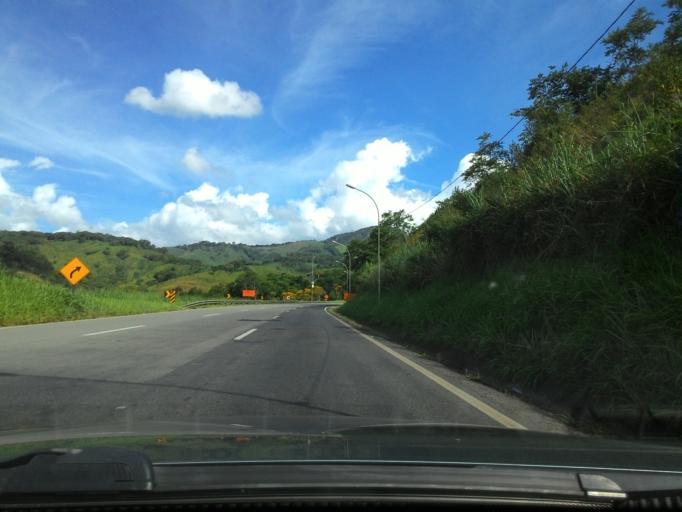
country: BR
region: Sao Paulo
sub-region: Cajati
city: Cajati
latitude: -24.8104
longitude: -48.2143
